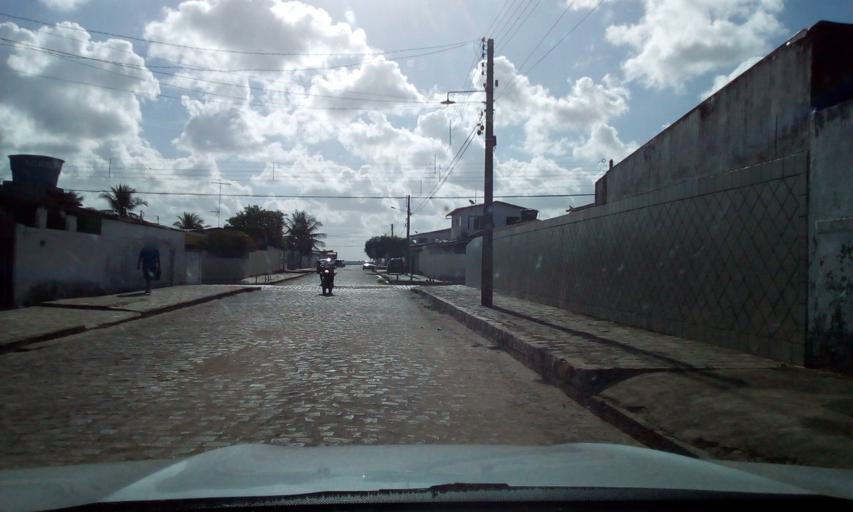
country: BR
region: Paraiba
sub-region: Bayeux
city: Bayeux
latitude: -7.1608
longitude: -34.8976
